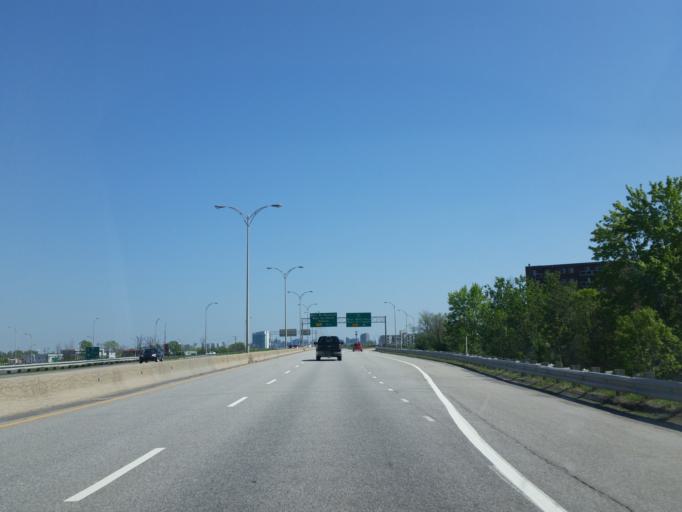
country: CA
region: Quebec
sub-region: Outaouais
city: Gatineau
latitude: 45.4657
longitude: -75.7450
